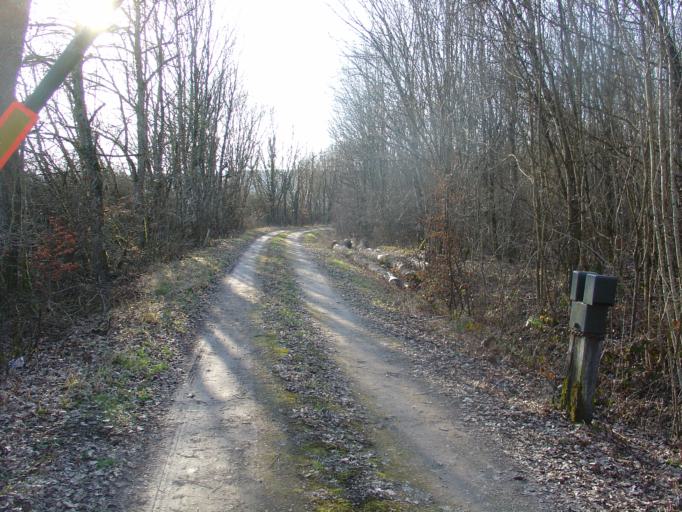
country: FR
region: Lorraine
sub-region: Departement de Meurthe-et-Moselle
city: Foug
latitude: 48.7346
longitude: 5.7919
